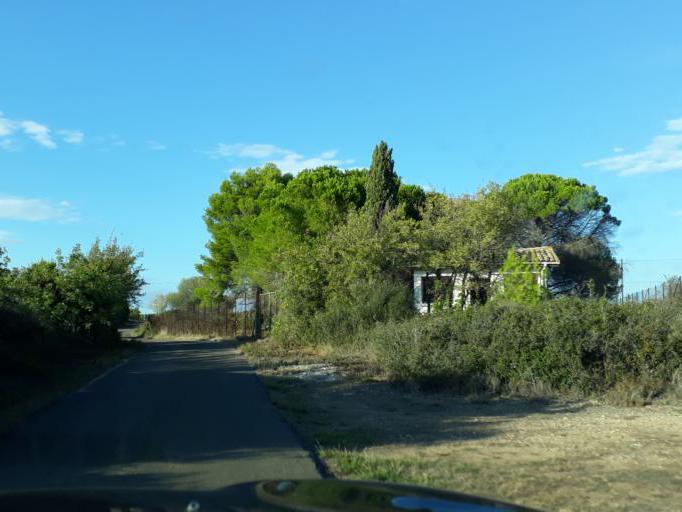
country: FR
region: Languedoc-Roussillon
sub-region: Departement de l'Herault
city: Florensac
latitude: 43.4187
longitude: 3.4737
